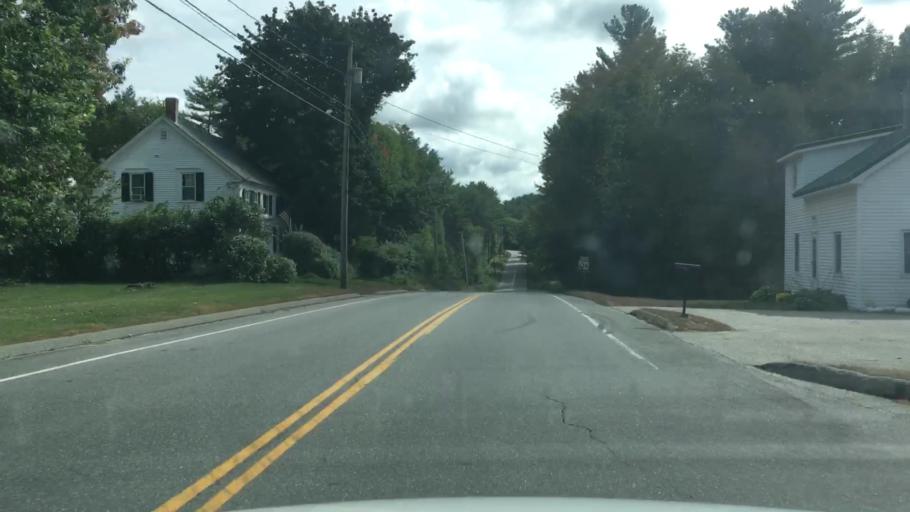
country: US
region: Maine
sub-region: Androscoggin County
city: Lewiston
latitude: 44.0512
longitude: -70.2002
